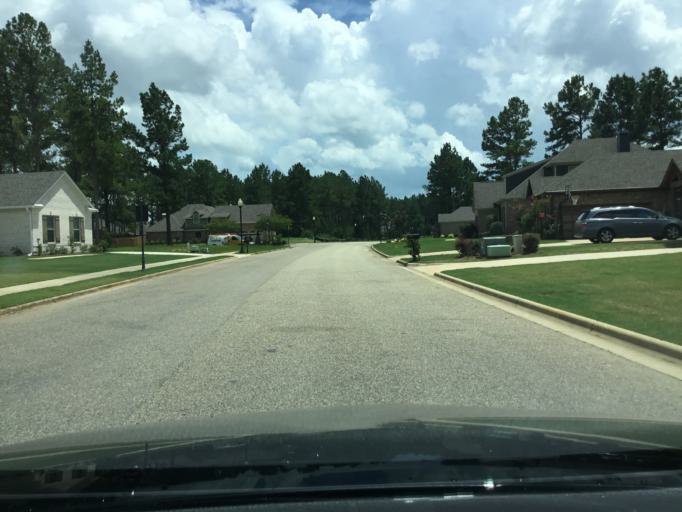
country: US
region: Alabama
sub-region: Montgomery County
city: Pike Road
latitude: 32.3421
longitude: -86.0803
